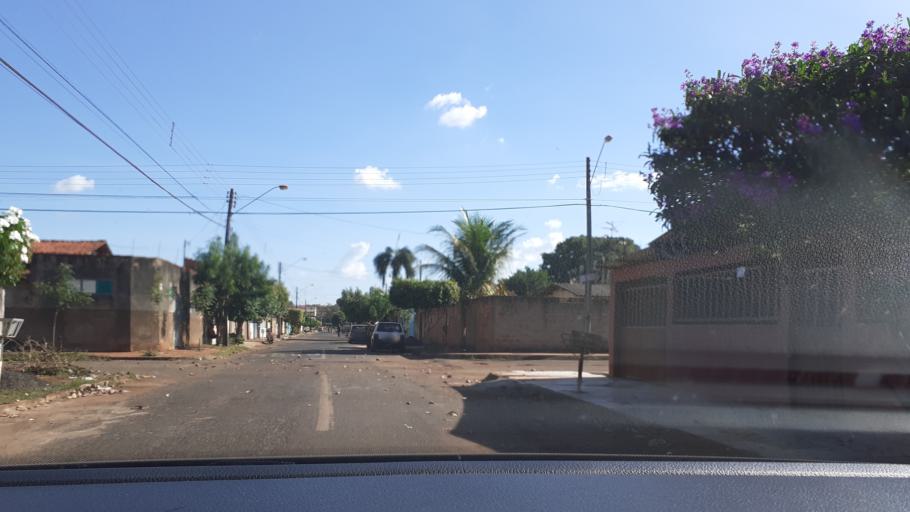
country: BR
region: Goias
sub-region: Itumbiara
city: Itumbiara
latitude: -18.4124
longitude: -49.2546
